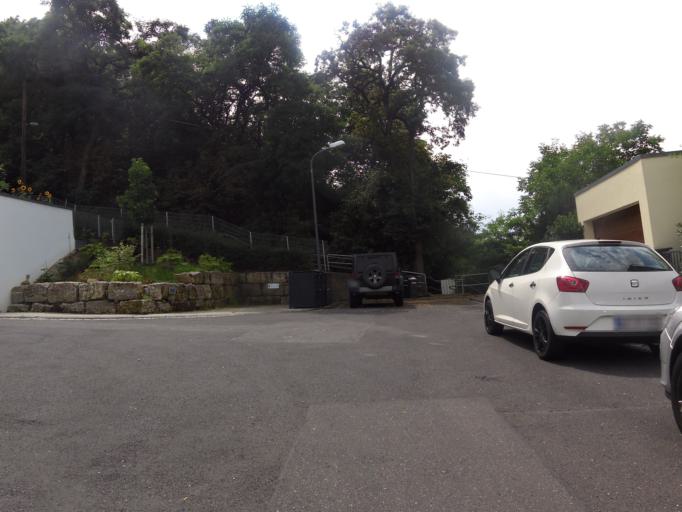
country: DE
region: Bavaria
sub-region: Regierungsbezirk Unterfranken
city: Hochberg
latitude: 49.7863
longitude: 9.8995
